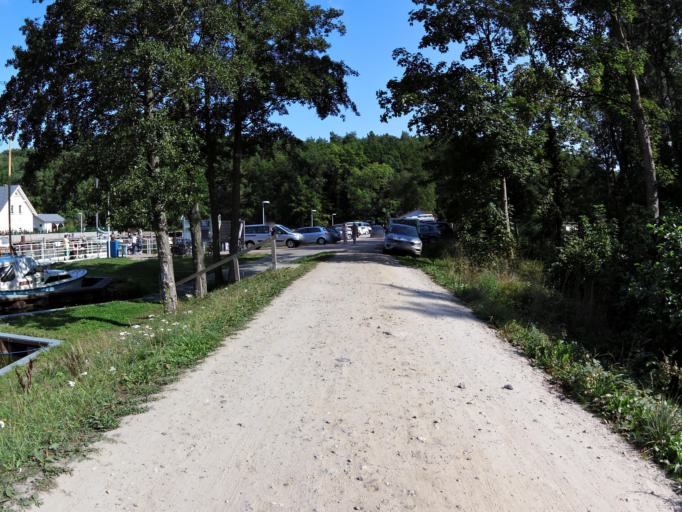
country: DE
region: Mecklenburg-Vorpommern
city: Loddin
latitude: 54.0006
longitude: 14.0460
